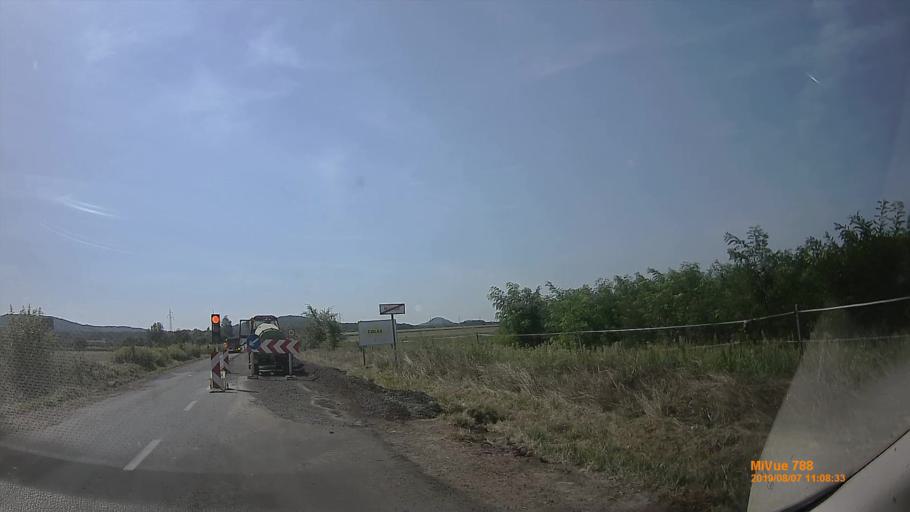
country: HU
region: Veszprem
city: Devecser
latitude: 46.9978
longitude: 17.4565
